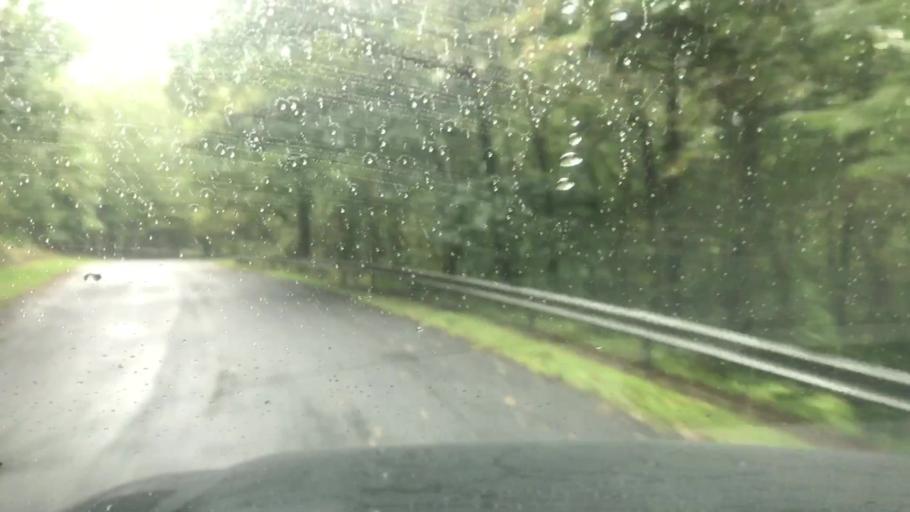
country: US
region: Pennsylvania
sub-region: Cumberland County
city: Shiremanstown
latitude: 40.1770
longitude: -76.9395
